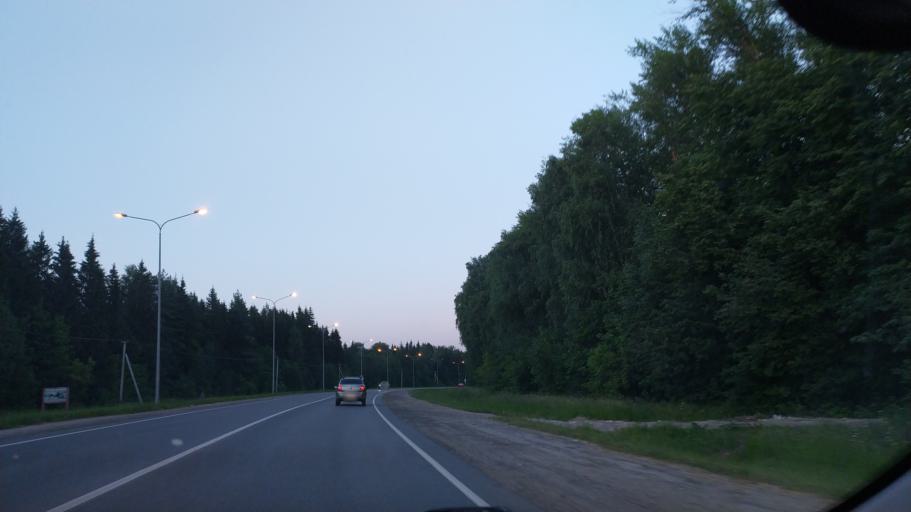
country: RU
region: Chuvashia
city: Ishley
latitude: 56.1348
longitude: 47.0926
